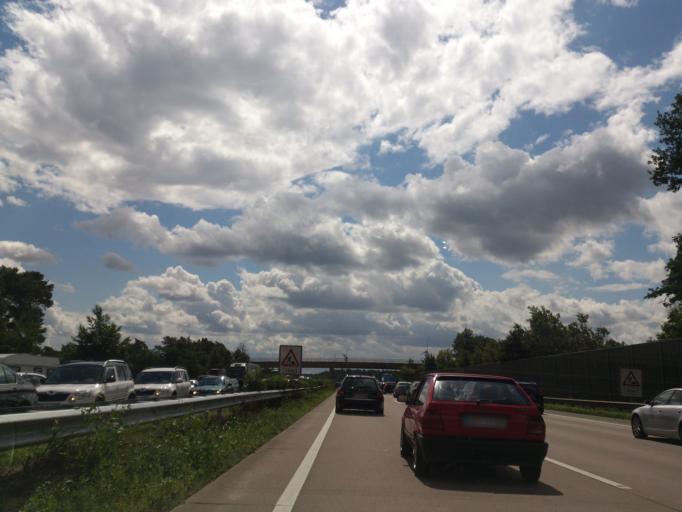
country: DE
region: Lower Saxony
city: Elze
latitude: 52.5978
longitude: 9.7484
